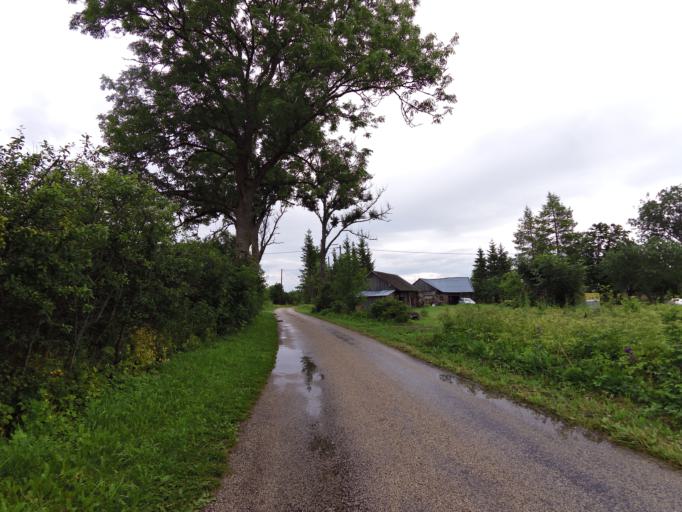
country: EE
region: Laeaene
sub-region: Vormsi vald
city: Hullo
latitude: 59.0190
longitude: 23.3066
